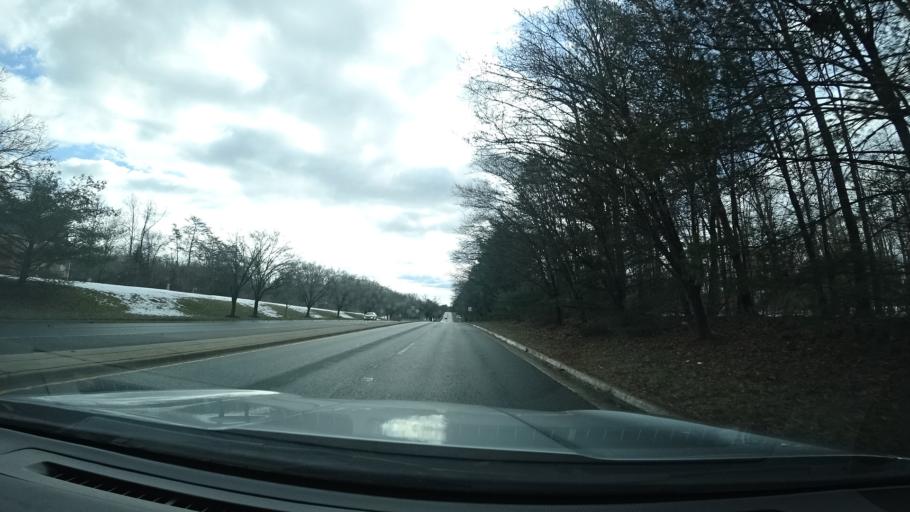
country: US
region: Virginia
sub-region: Loudoun County
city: Sugarland Run
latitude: 39.0206
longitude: -77.3627
